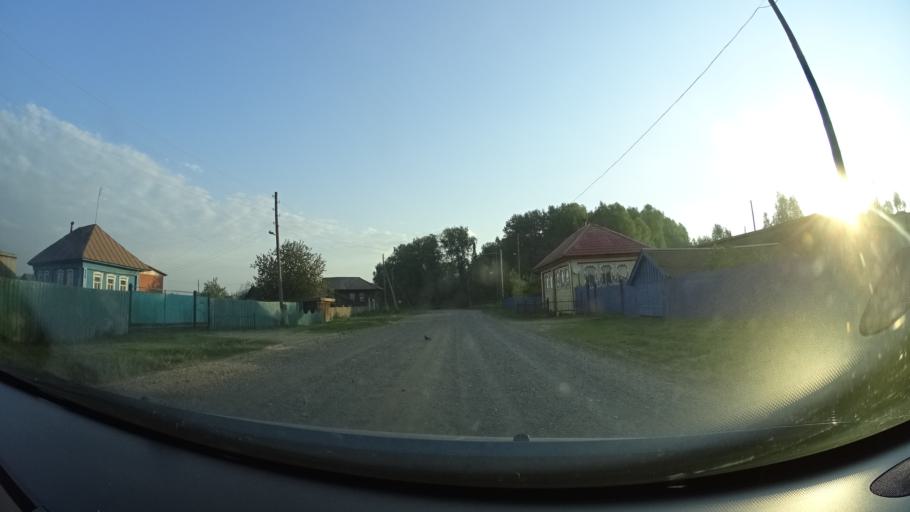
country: RU
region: Perm
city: Barda
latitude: 56.6804
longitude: 55.6907
